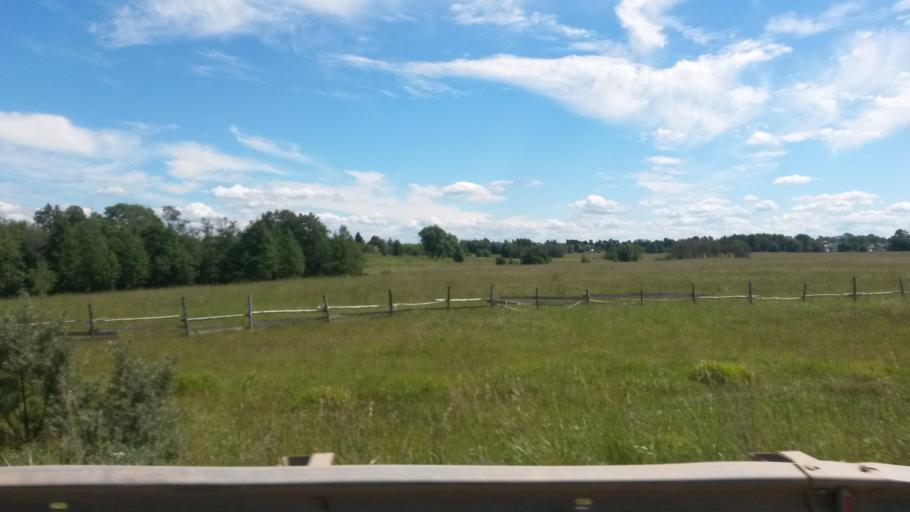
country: RU
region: Ivanovo
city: Staraya Vichuga
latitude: 57.2354
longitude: 41.8776
